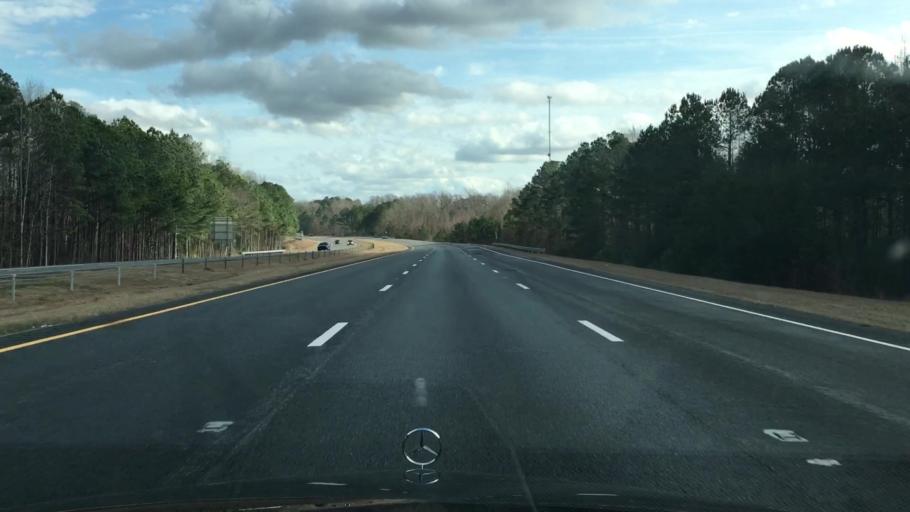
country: US
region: North Carolina
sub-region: Johnston County
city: Benson
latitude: 35.3280
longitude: -78.4445
